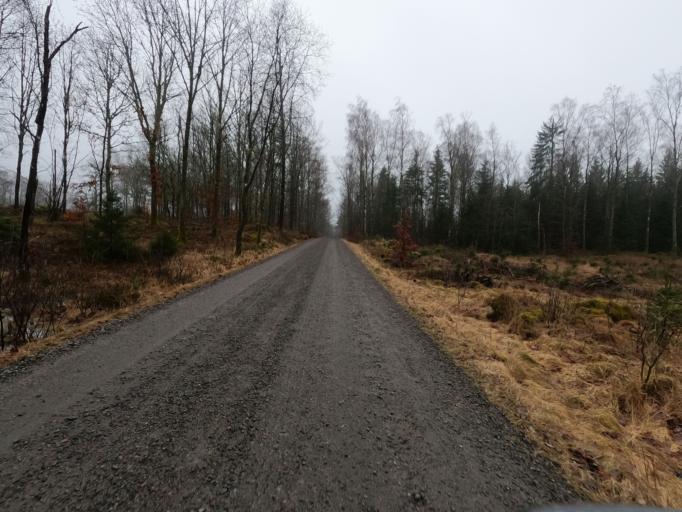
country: SE
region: Halland
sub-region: Hylte Kommun
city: Hyltebruk
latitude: 56.8104
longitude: 13.3198
